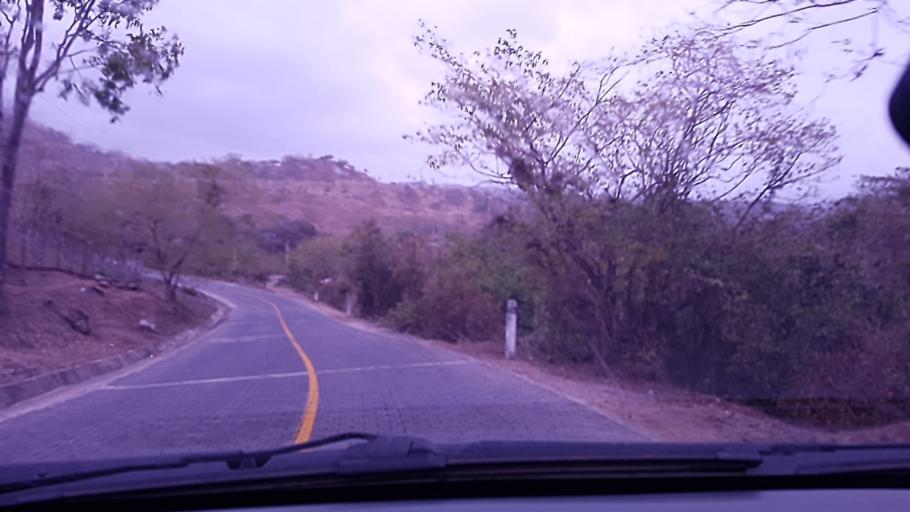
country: NI
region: Jinotega
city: La Concordia
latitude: 13.1664
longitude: -86.1719
